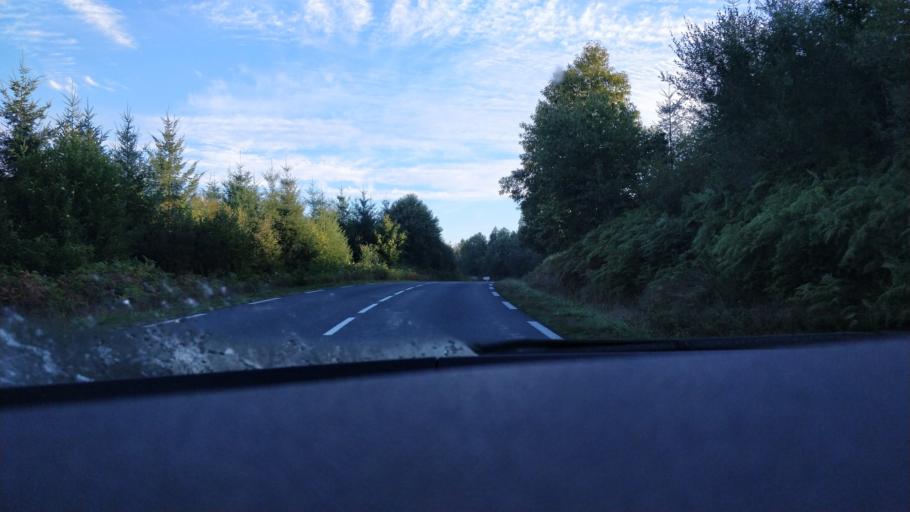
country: FR
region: Limousin
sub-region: Departement de la Haute-Vienne
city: Sauviat-sur-Vige
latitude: 45.9293
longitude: 1.6504
